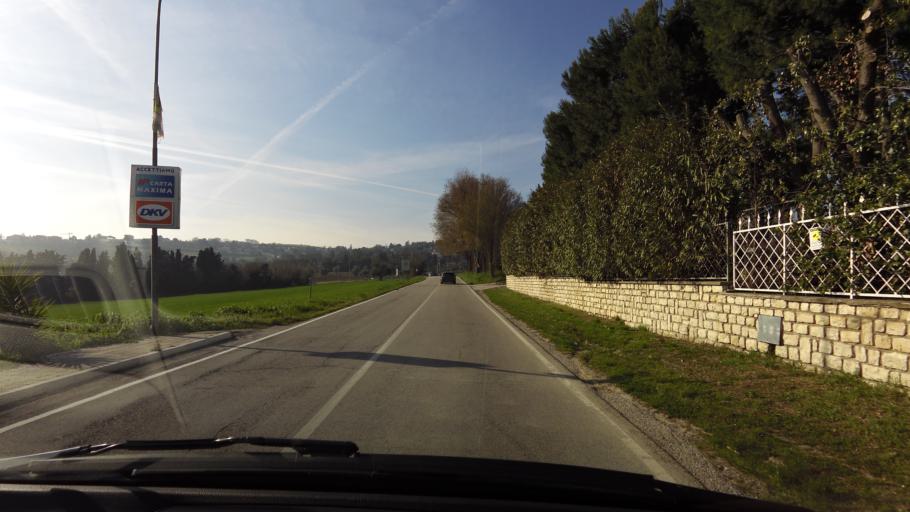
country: IT
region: The Marches
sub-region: Provincia di Ancona
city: Marcelli
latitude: 43.4985
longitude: 13.6192
